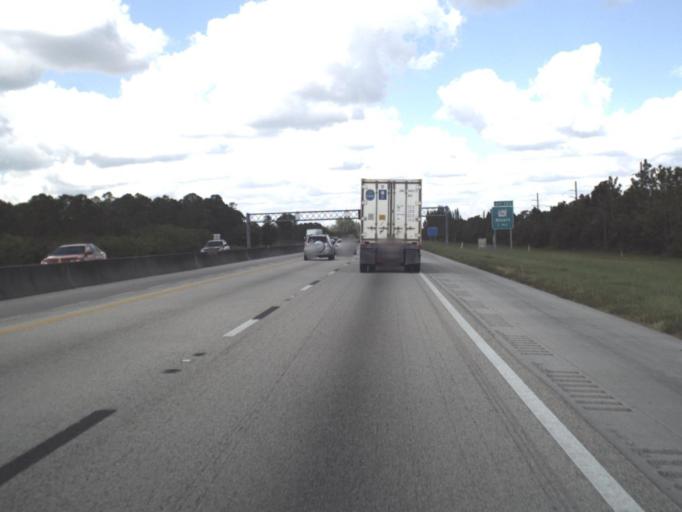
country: US
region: Florida
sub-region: Martin County
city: Palm City
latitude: 27.1432
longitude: -80.2922
